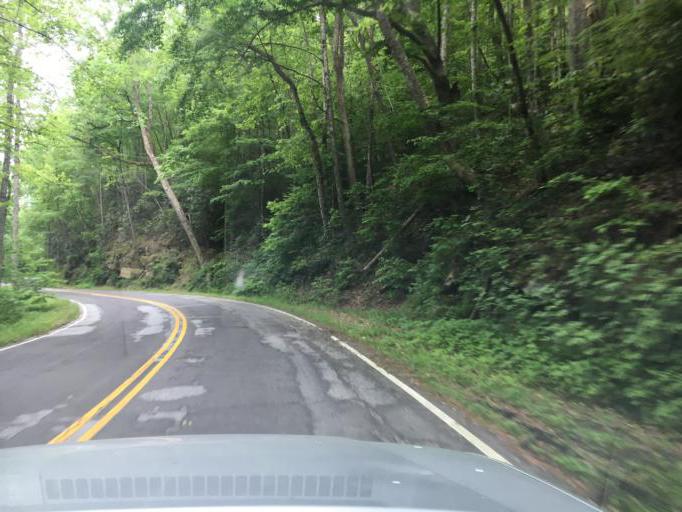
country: US
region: North Carolina
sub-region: Henderson County
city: Flat Rock
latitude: 35.1784
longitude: -82.4074
